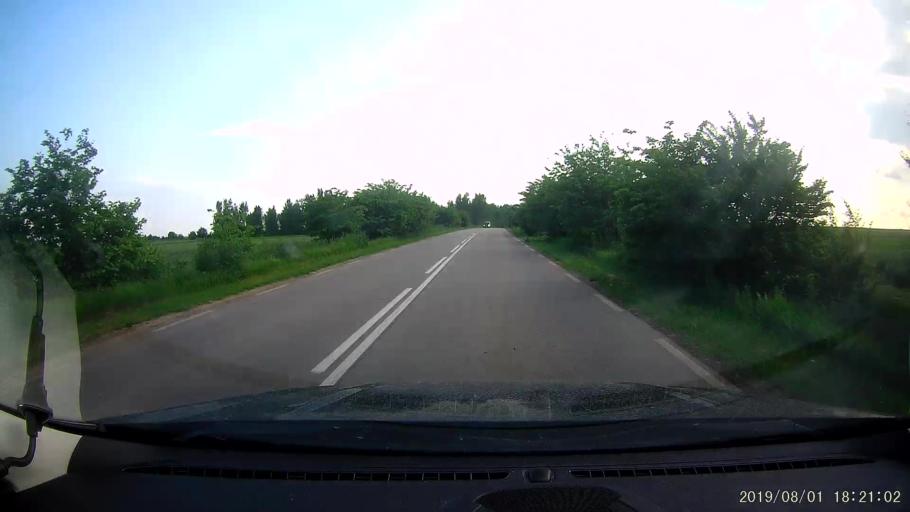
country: BG
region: Shumen
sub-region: Obshtina Kaolinovo
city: Kaolinovo
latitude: 43.6590
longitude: 27.0787
